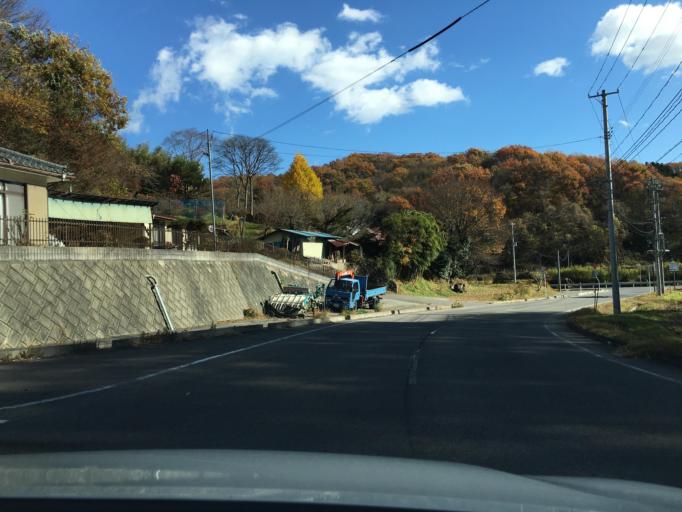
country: JP
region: Fukushima
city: Miharu
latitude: 37.4476
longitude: 140.4671
